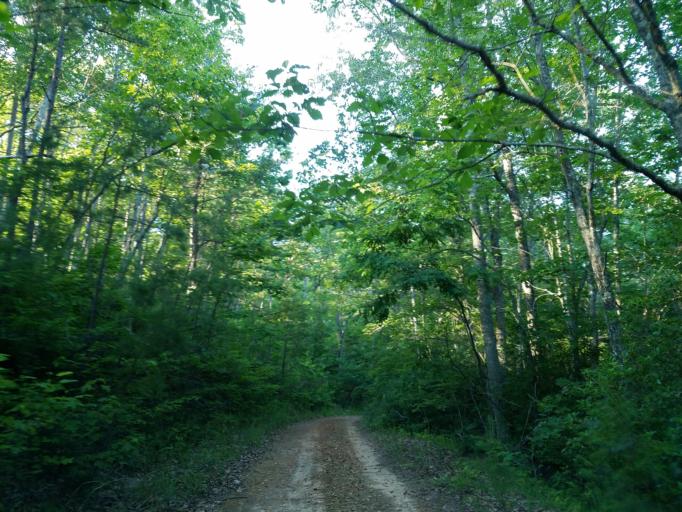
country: US
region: Georgia
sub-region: Fannin County
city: Blue Ridge
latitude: 34.8132
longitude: -84.1528
